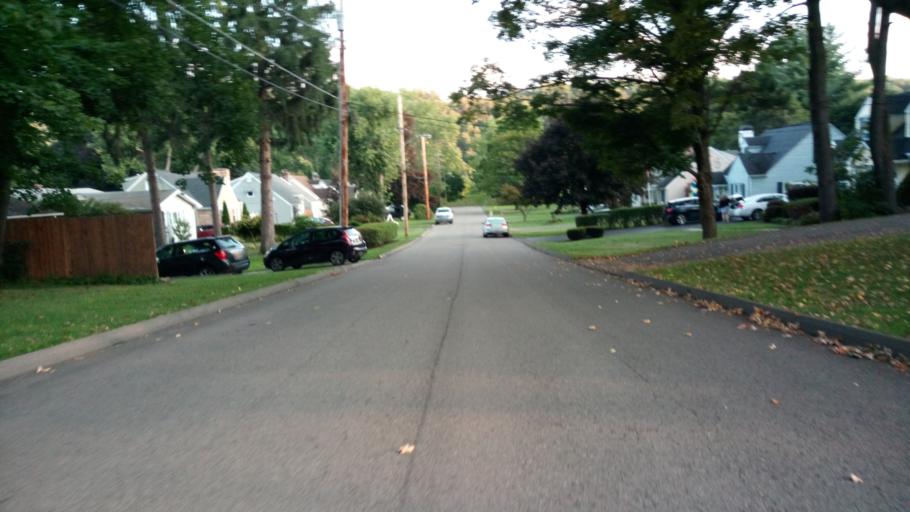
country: US
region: New York
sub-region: Chemung County
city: West Elmira
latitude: 42.0779
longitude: -76.8374
